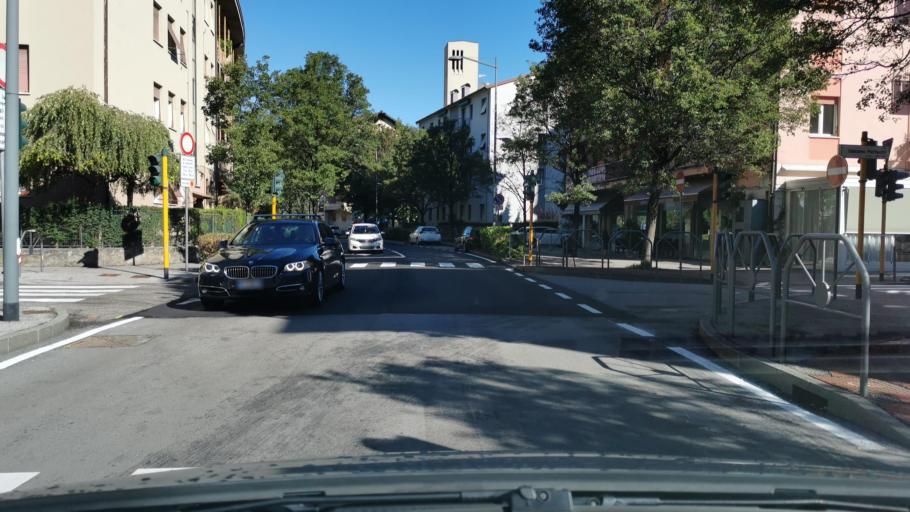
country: IT
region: Trentino-Alto Adige
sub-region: Provincia di Trento
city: Trento
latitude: 46.0557
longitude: 11.1201
